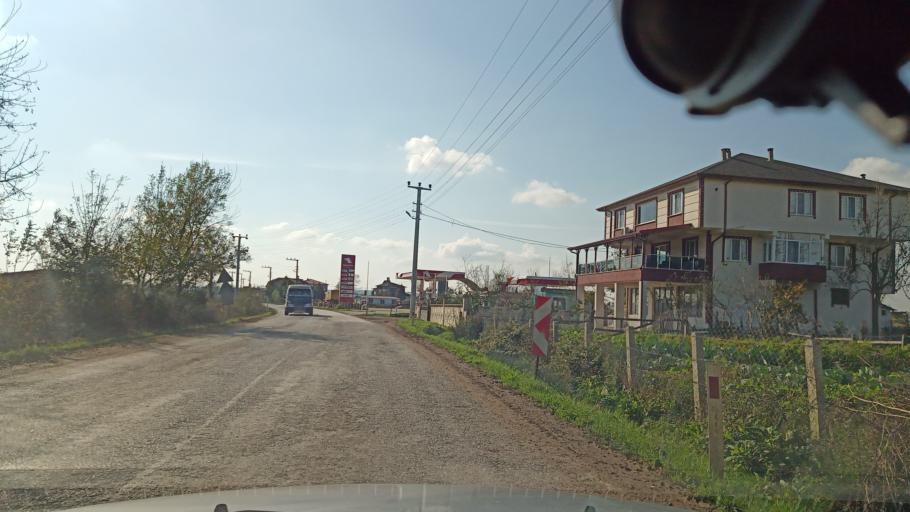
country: TR
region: Sakarya
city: Kaynarca
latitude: 41.0989
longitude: 30.4323
